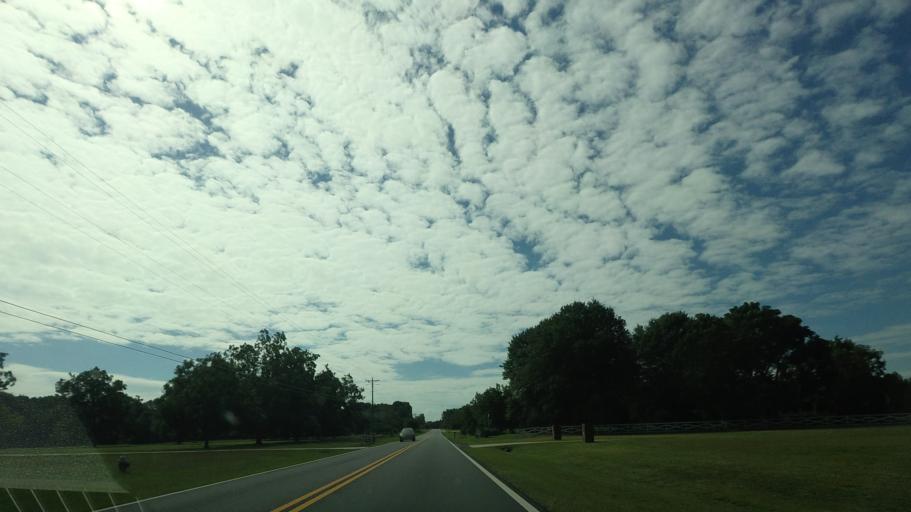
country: US
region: Georgia
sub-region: Houston County
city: Centerville
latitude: 32.6547
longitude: -83.6967
